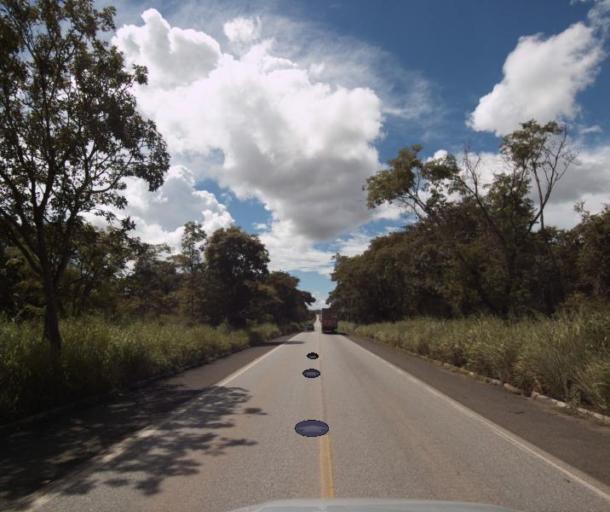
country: BR
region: Goias
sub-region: Uruacu
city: Uruacu
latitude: -14.0666
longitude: -49.0946
